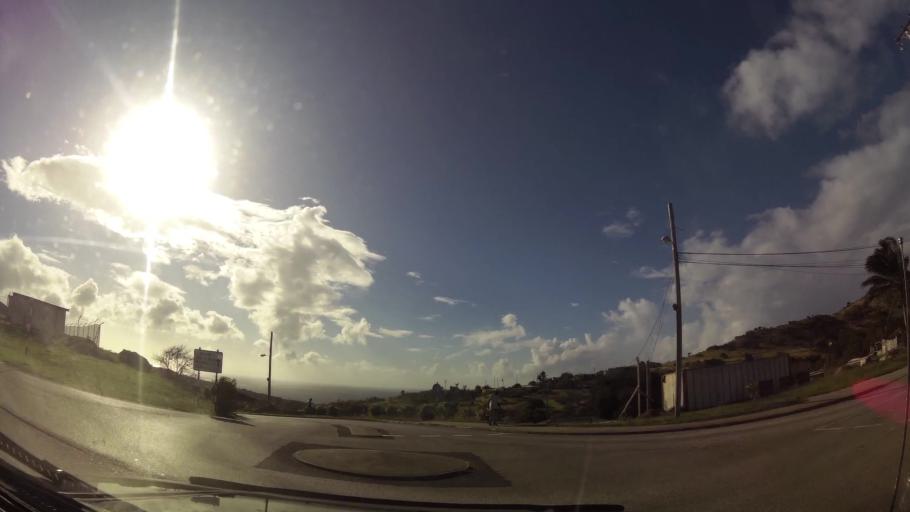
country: MS
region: Saint Peter
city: Brades
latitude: 16.7929
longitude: -62.1944
